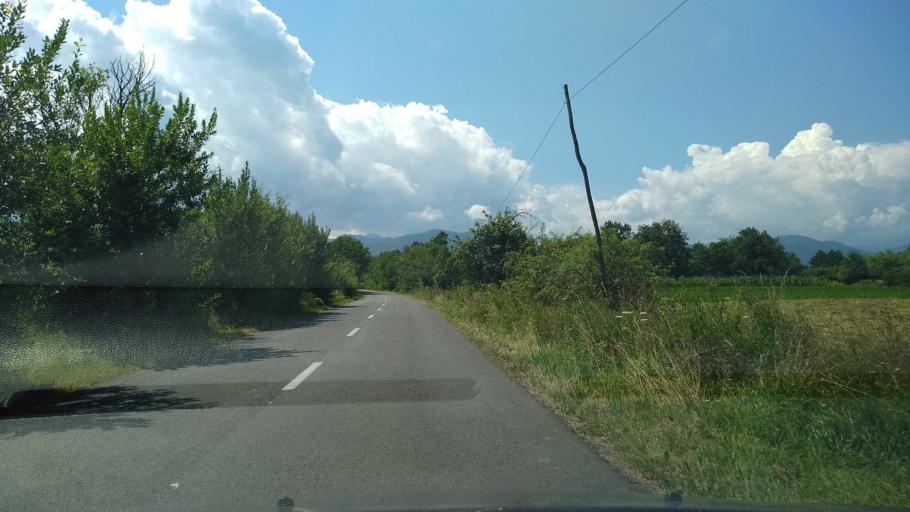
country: RO
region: Hunedoara
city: Salasu de Sus
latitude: 45.5171
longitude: 22.9588
